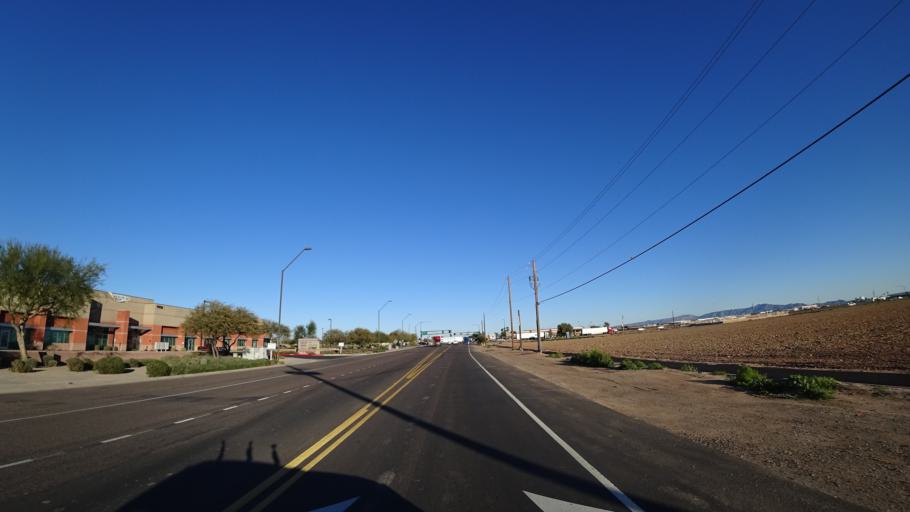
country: US
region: Arizona
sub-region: Maricopa County
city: Tolleson
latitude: 33.4502
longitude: -112.2751
